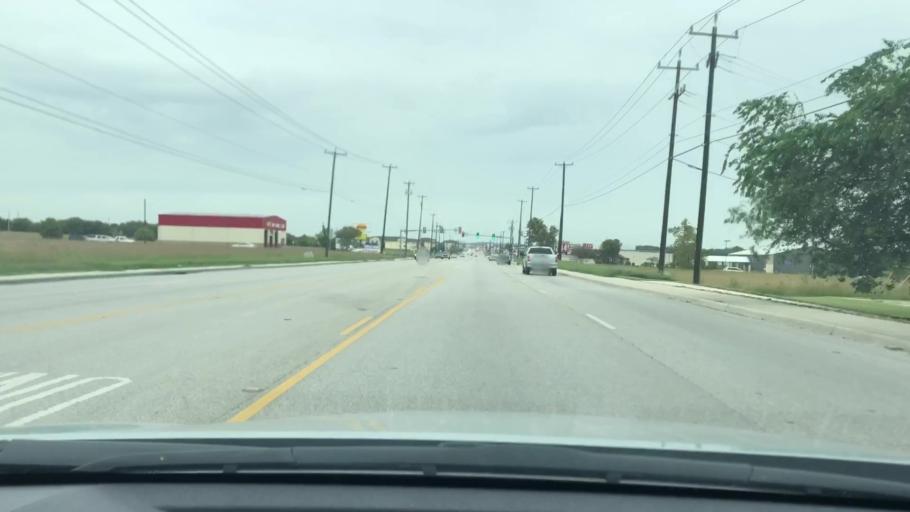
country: US
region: Texas
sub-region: Bexar County
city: Kirby
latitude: 29.4660
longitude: -98.3594
